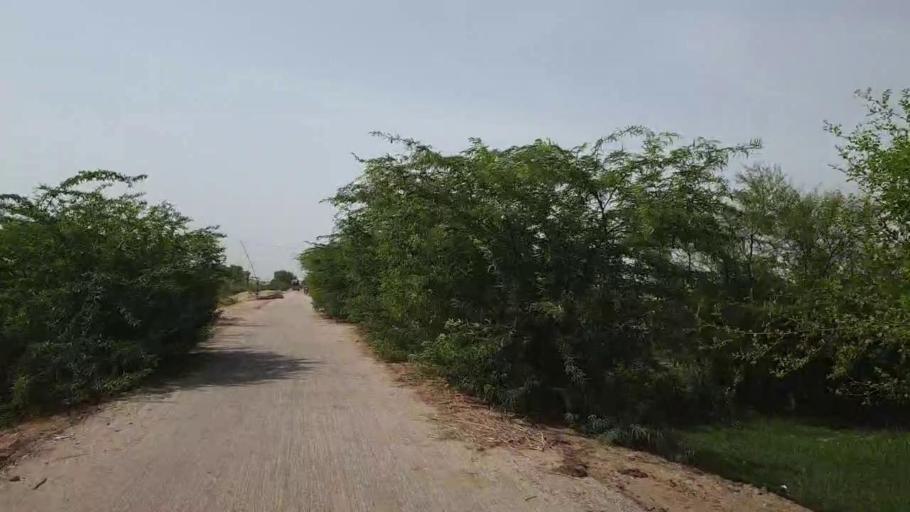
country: PK
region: Sindh
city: Bandhi
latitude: 26.5513
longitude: 68.3840
